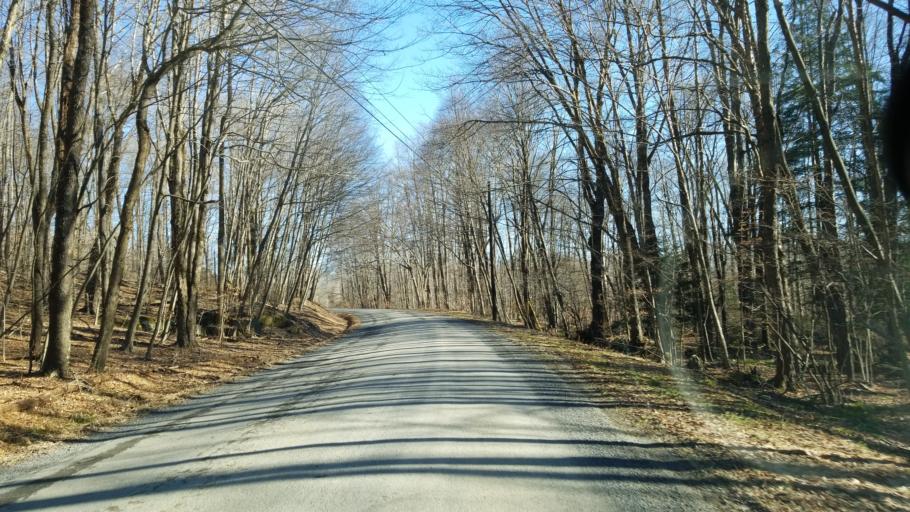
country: US
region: Pennsylvania
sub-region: Jefferson County
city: Falls Creek
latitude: 41.1590
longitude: -78.8341
